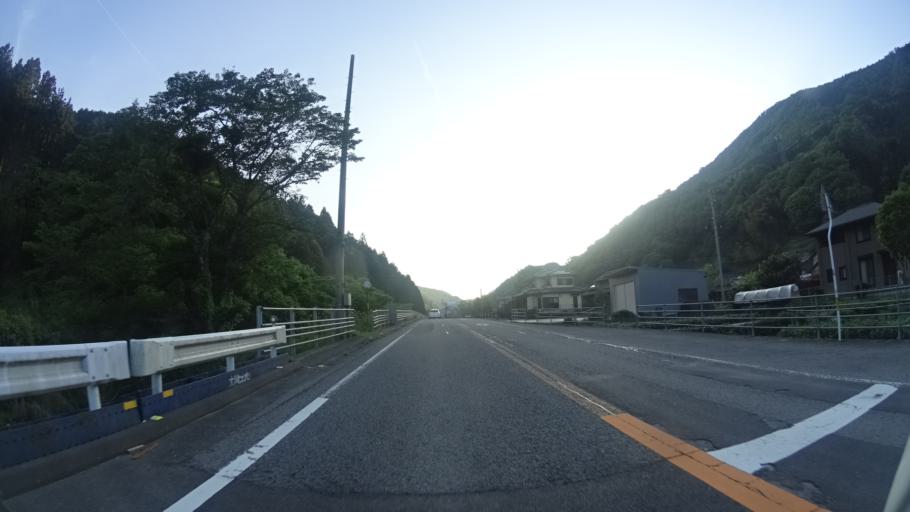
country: JP
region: Tokushima
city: Ikedacho
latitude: 34.0118
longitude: 133.7485
